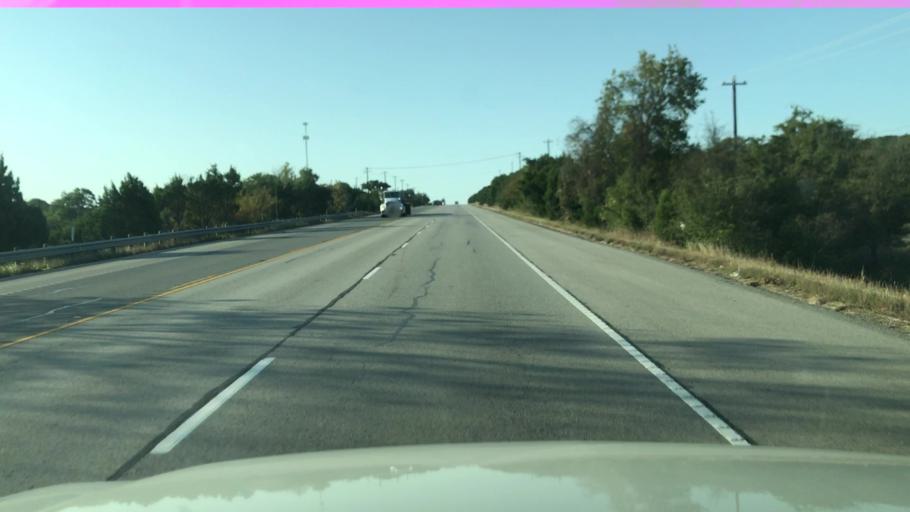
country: US
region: Texas
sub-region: Blanco County
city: Blanco
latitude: 30.1817
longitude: -98.3793
